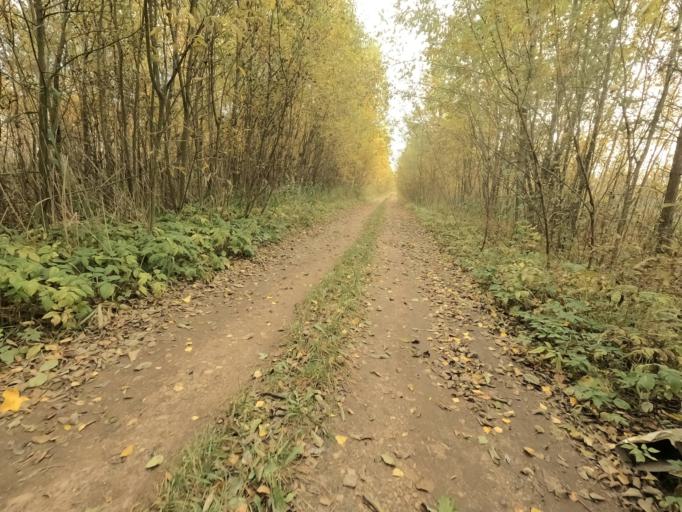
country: RU
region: Novgorod
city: Pankovka
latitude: 58.8755
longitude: 30.8750
